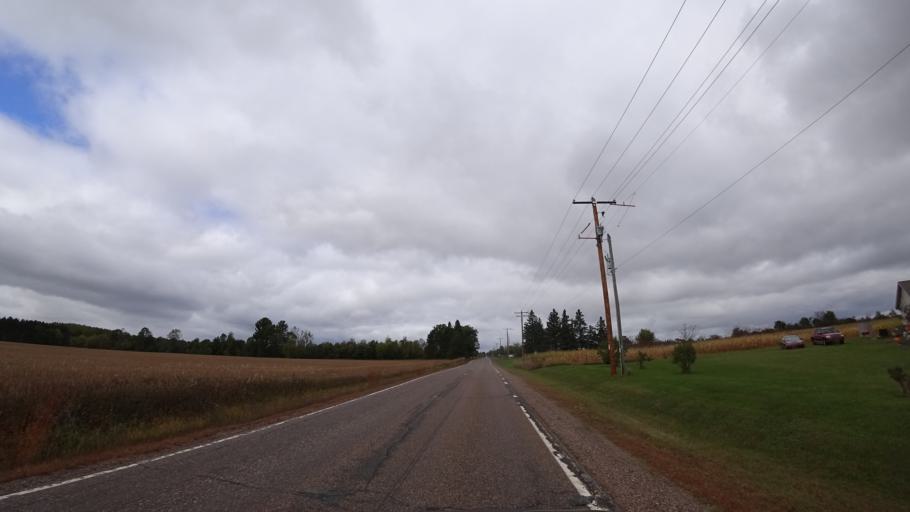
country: US
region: Wisconsin
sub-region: Chippewa County
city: Lake Wissota
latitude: 44.9679
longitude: -91.2678
